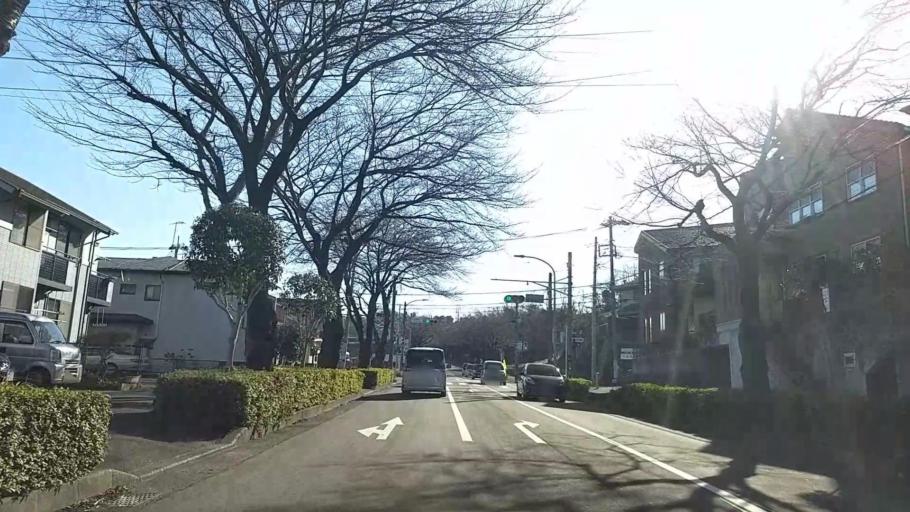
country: JP
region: Kanagawa
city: Hadano
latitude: 35.3636
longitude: 139.2146
